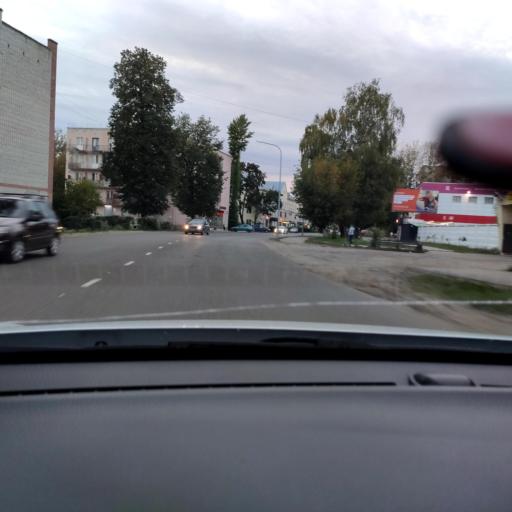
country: RU
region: Mariy-El
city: Volzhsk
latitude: 55.8597
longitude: 48.3819
